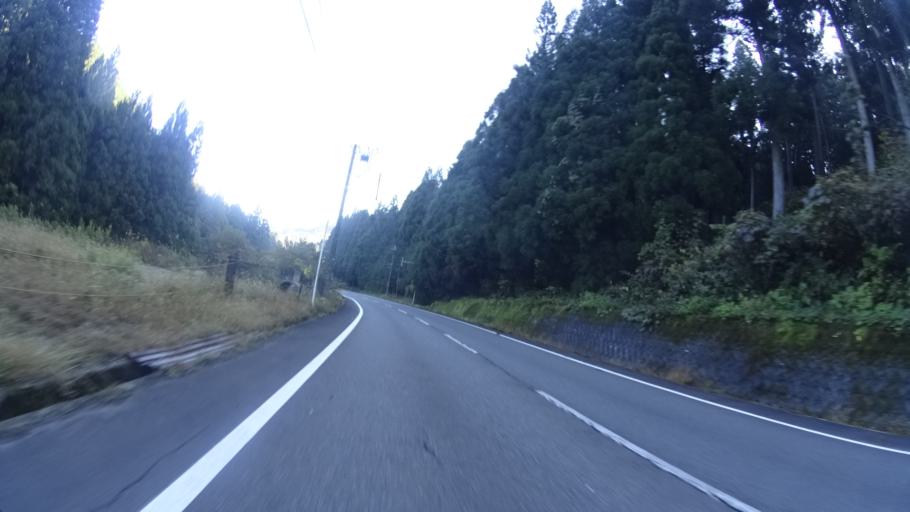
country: JP
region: Fukui
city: Maruoka
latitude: 36.1513
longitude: 136.3305
